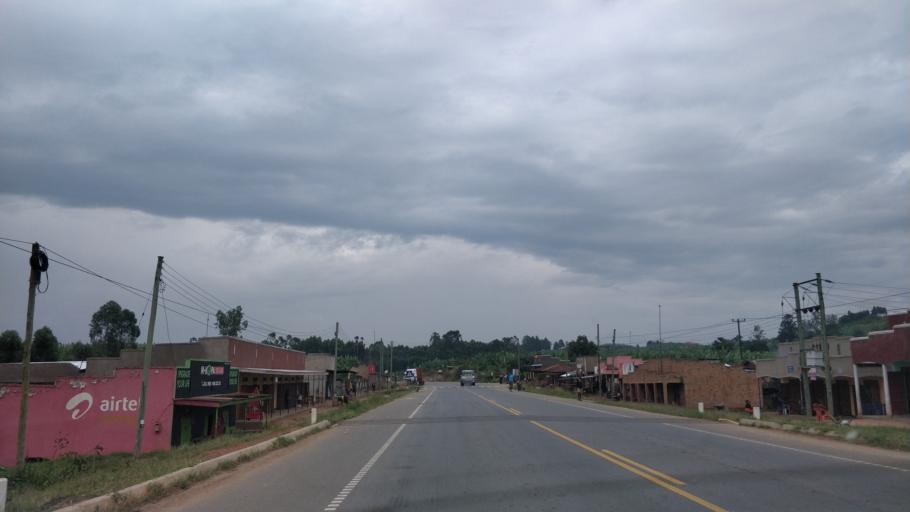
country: UG
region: Western Region
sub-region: Sheema District
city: Kibingo
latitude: -0.6682
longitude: 30.4430
